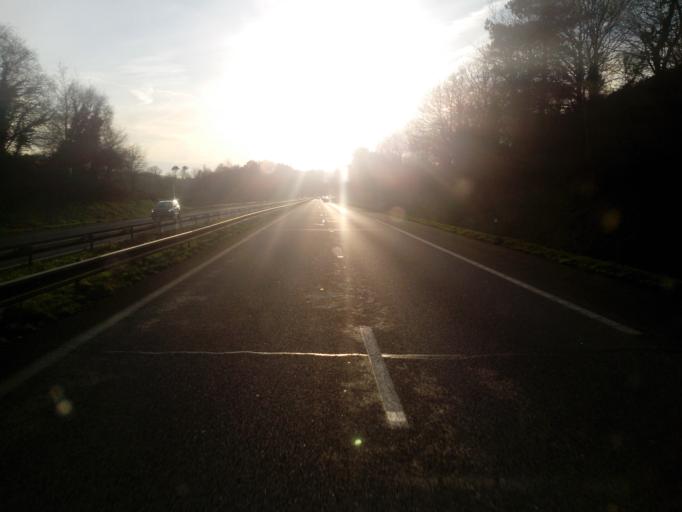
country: FR
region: Brittany
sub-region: Departement du Morbihan
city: Languidic
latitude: 47.8492
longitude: -3.1238
